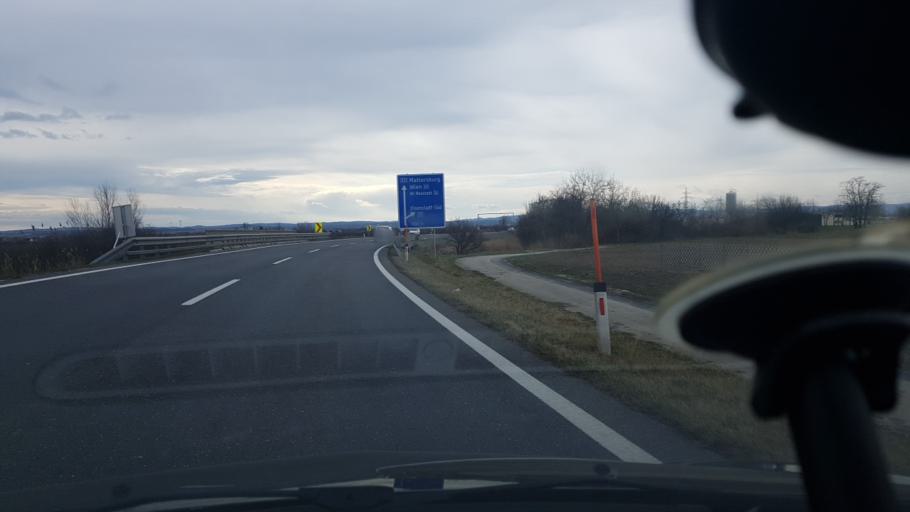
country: AT
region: Burgenland
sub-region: Eisenstadt-Umgebung
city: Trausdorf an der Wulka
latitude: 47.8314
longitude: 16.5510
